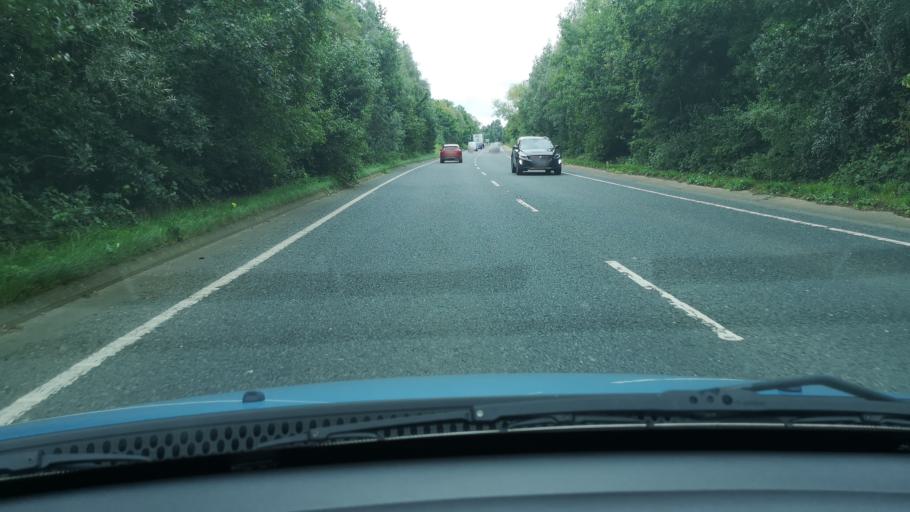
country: GB
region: England
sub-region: City and Borough of Wakefield
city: Hemsworth
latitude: 53.6012
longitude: -1.3686
